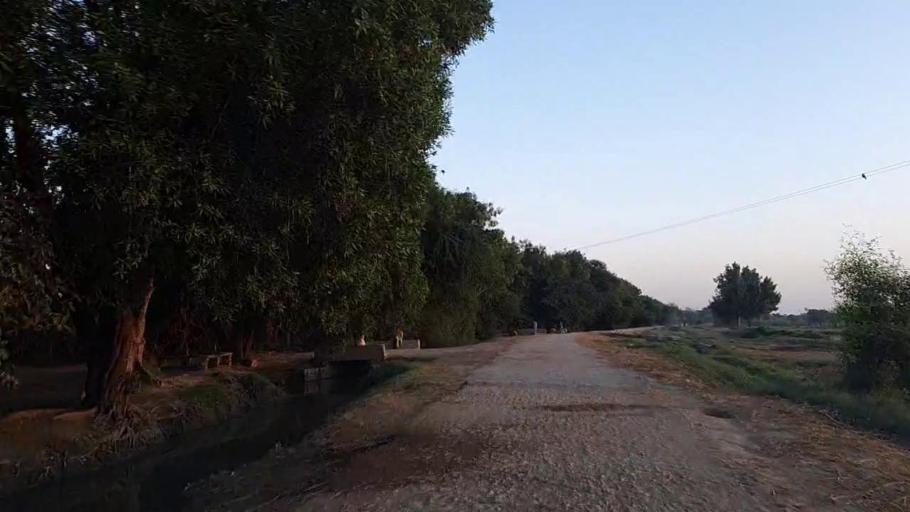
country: PK
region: Sindh
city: Mirpur Batoro
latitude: 24.6393
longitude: 68.1899
